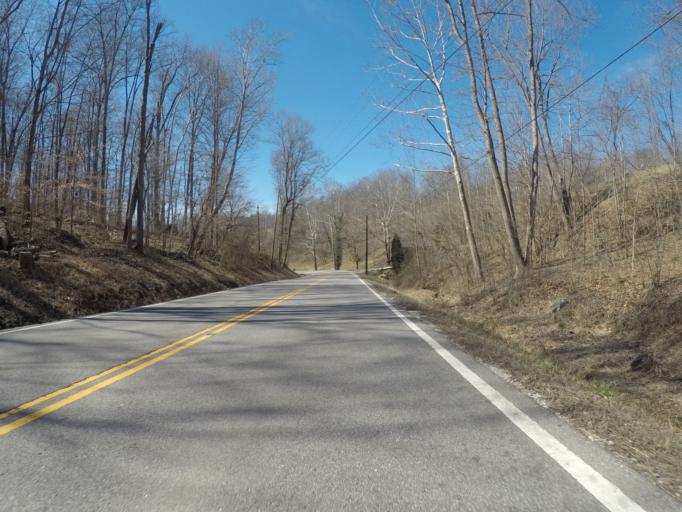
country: US
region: Ohio
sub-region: Lawrence County
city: South Point
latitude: 38.4872
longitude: -82.5580
